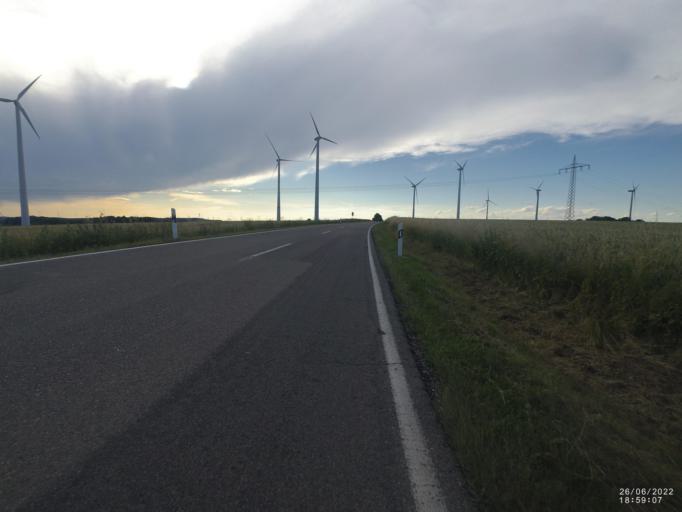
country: DE
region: Baden-Wuerttemberg
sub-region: Regierungsbezirk Stuttgart
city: Bohmenkirch
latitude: 48.6528
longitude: 9.9398
